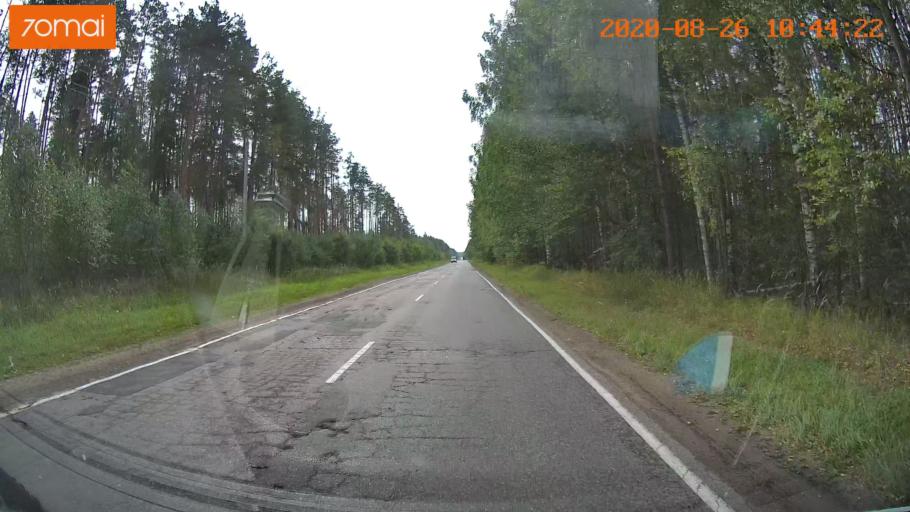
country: RU
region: Rjazan
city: Lashma
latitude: 54.7710
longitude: 41.1832
